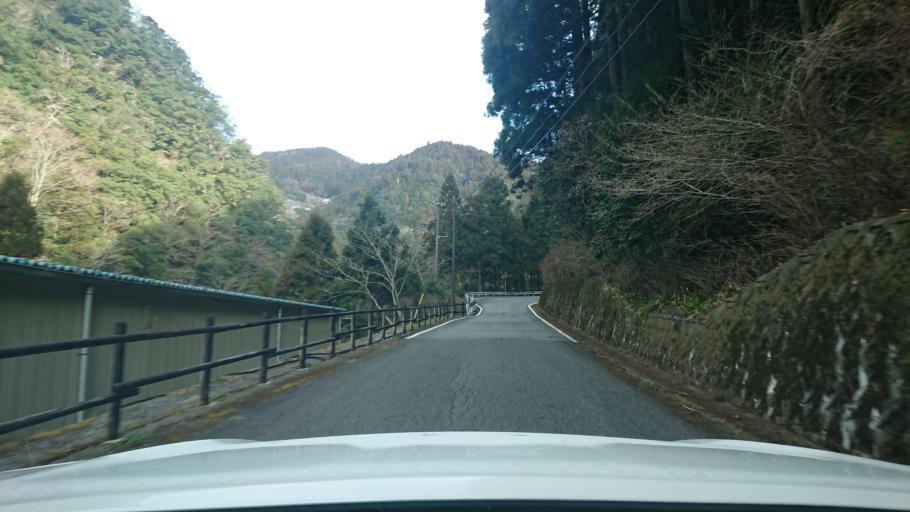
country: JP
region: Tokushima
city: Kamojimacho-jogejima
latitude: 33.9077
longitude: 134.3941
